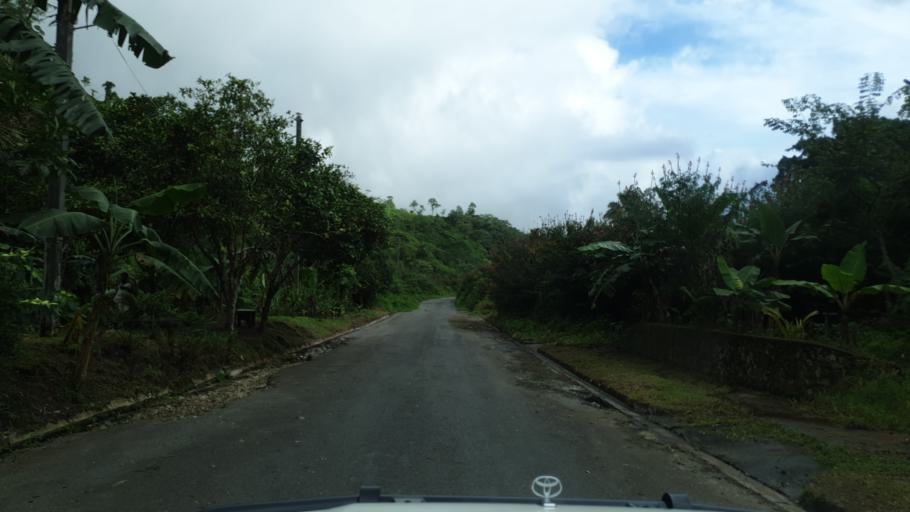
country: PG
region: Bougainville
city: Panguna
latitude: -6.3000
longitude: 155.4928
